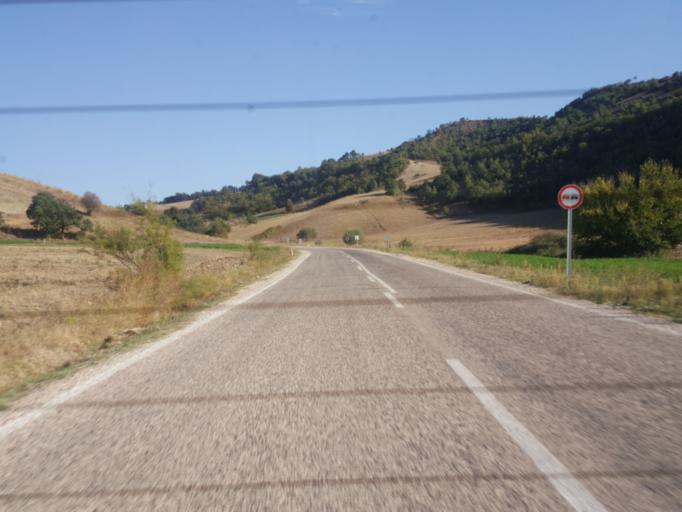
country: TR
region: Amasya
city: Tasova
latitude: 40.7200
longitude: 36.3041
